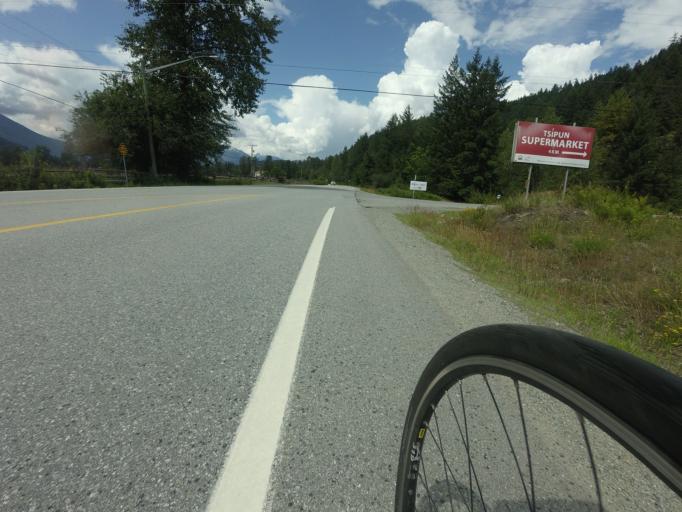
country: CA
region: British Columbia
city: Pemberton
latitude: 50.3092
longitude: -122.6524
